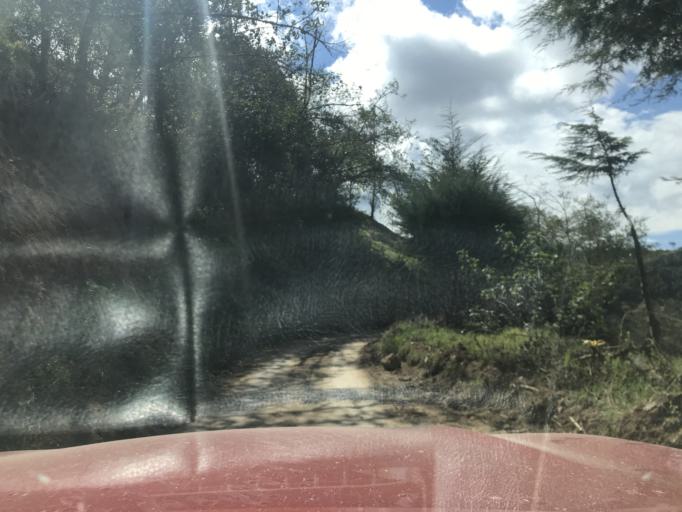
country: PE
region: Cajamarca
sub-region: Provincia de Chota
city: Querocoto
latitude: -6.3509
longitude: -79.0418
